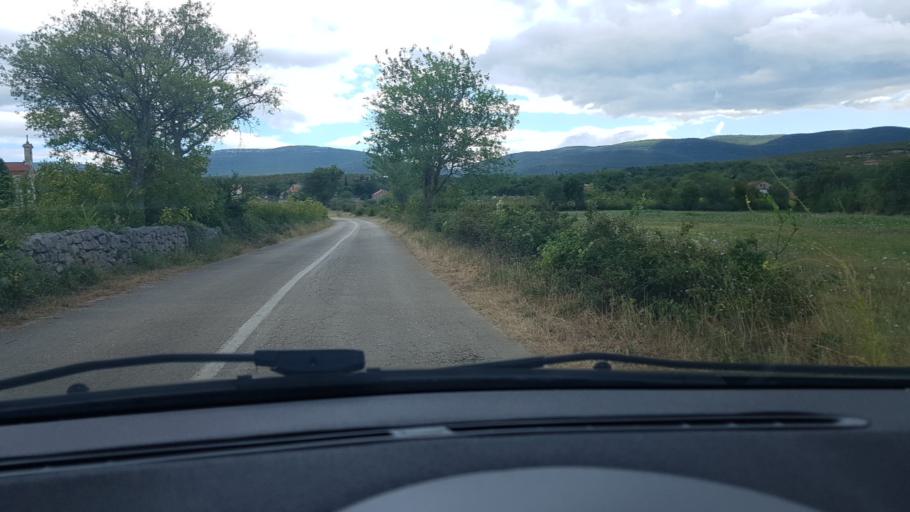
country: HR
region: Zadarska
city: Gracac
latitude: 44.1609
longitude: 15.8582
